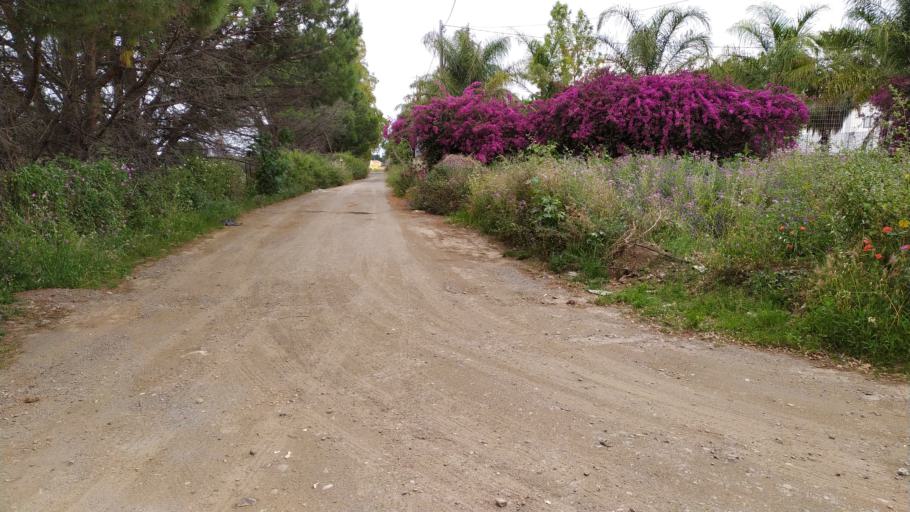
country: IT
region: Sicily
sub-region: Messina
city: San Filippo del Mela
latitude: 38.1870
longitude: 15.2646
